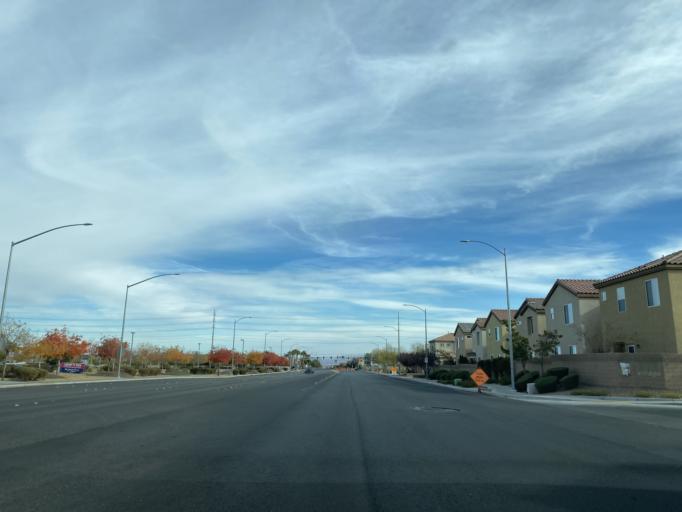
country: US
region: Nevada
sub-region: Clark County
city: Enterprise
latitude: 36.0411
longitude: -115.2471
